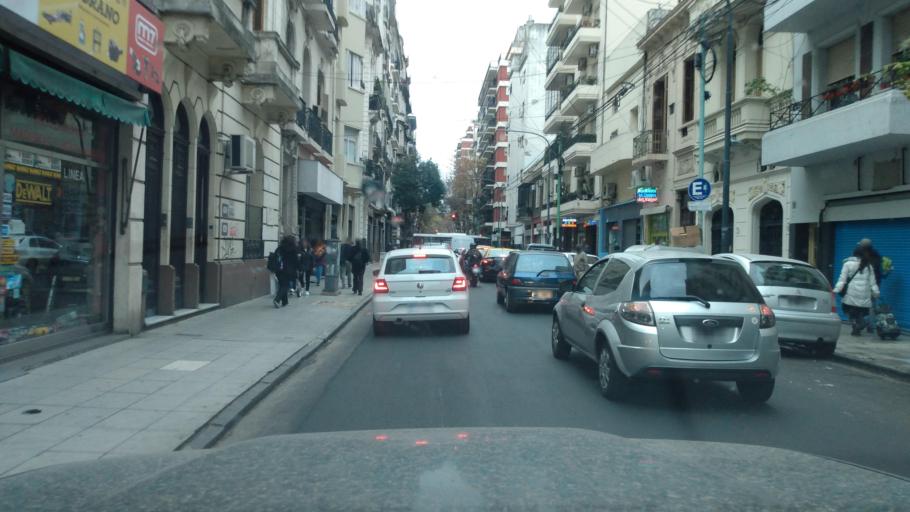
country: AR
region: Buenos Aires F.D.
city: Buenos Aires
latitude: -34.6075
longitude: -58.3965
